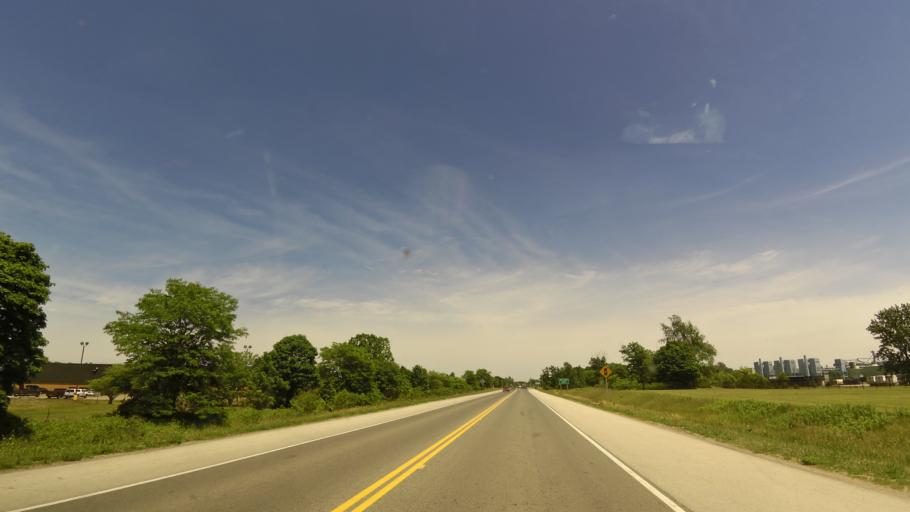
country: CA
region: Ontario
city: Ingersoll
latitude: 42.8504
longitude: -80.7097
